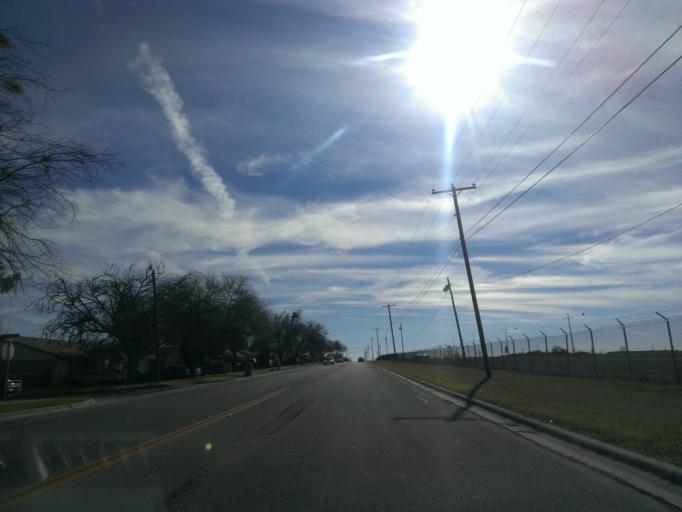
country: US
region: Texas
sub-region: Bell County
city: Killeen
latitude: 31.1383
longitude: -97.7036
